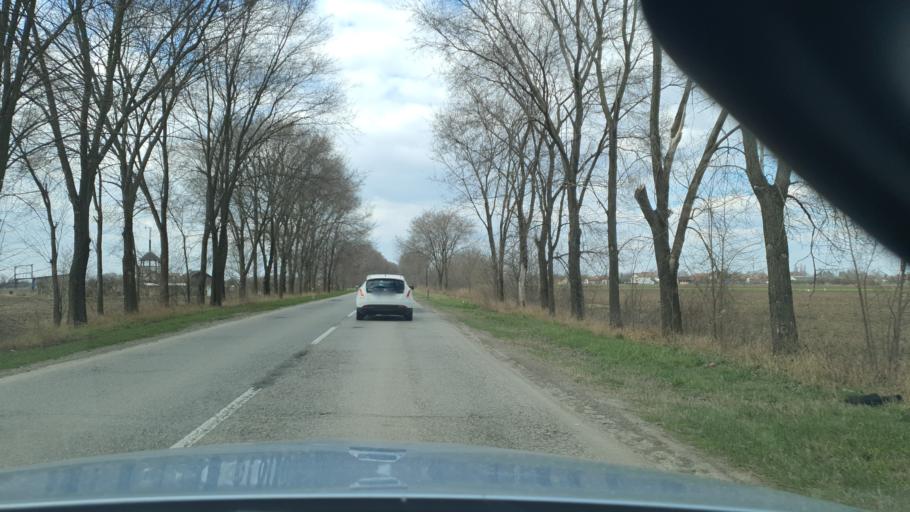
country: RS
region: Autonomna Pokrajina Vojvodina
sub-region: Zapadnobacki Okrug
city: Odzaci
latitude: 45.4493
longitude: 19.3517
